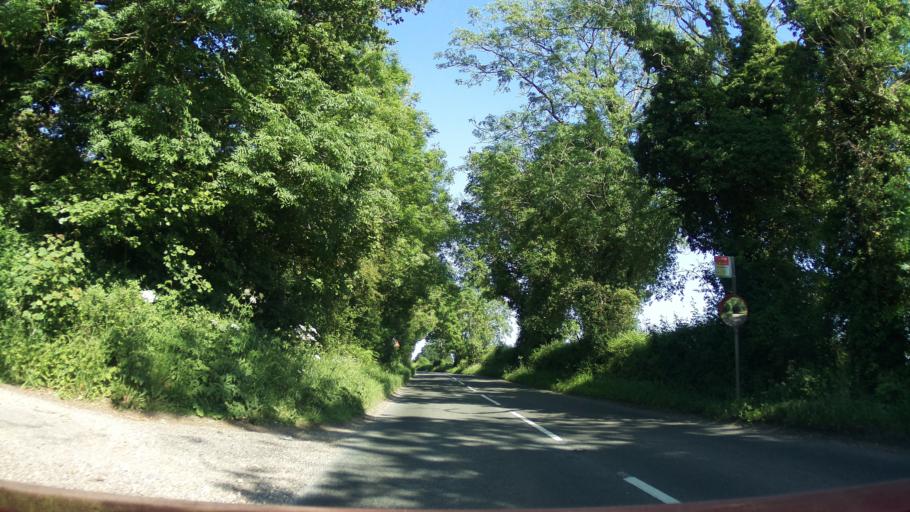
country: GB
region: England
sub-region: Hampshire
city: Andover
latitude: 51.2148
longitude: -1.3885
